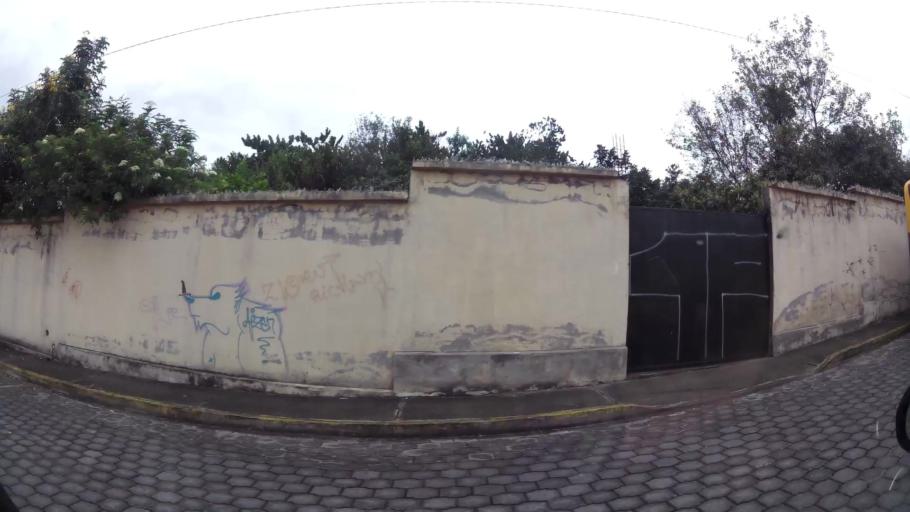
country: EC
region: Pichincha
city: Sangolqui
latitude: -0.3047
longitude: -78.4737
